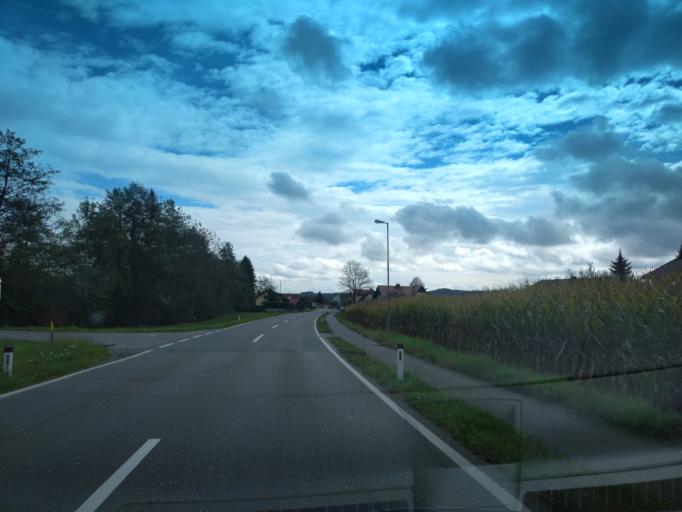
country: AT
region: Styria
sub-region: Politischer Bezirk Deutschlandsberg
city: Rassach
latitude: 46.8252
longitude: 15.2741
